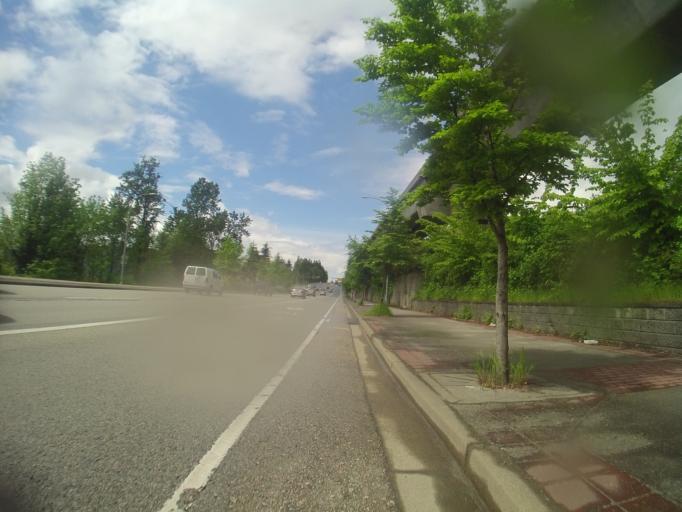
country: CA
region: British Columbia
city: Burnaby
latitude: 49.2528
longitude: -122.9147
